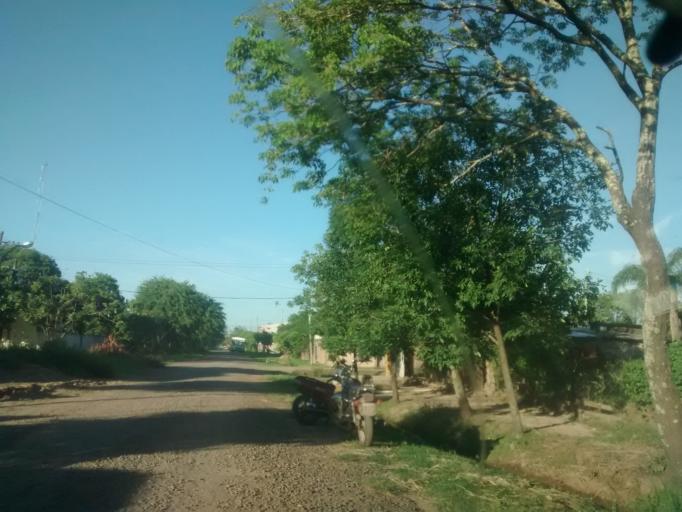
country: AR
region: Chaco
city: Resistencia
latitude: -27.4510
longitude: -59.0079
